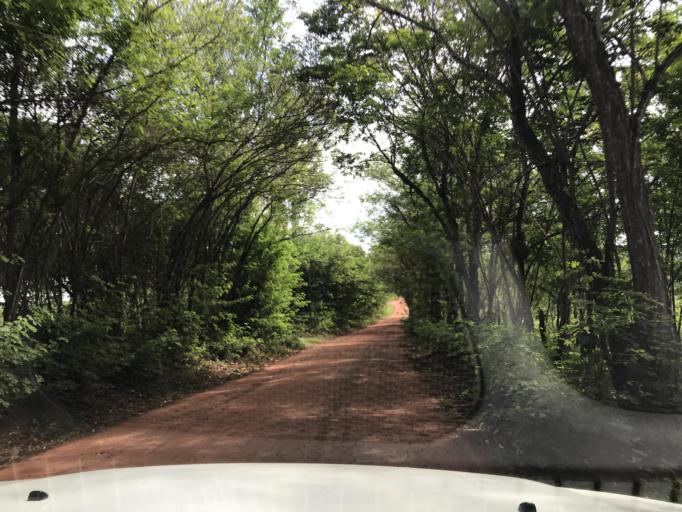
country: BR
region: Bahia
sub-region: Entre Rios
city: Entre Rios
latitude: -12.1763
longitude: -38.1199
